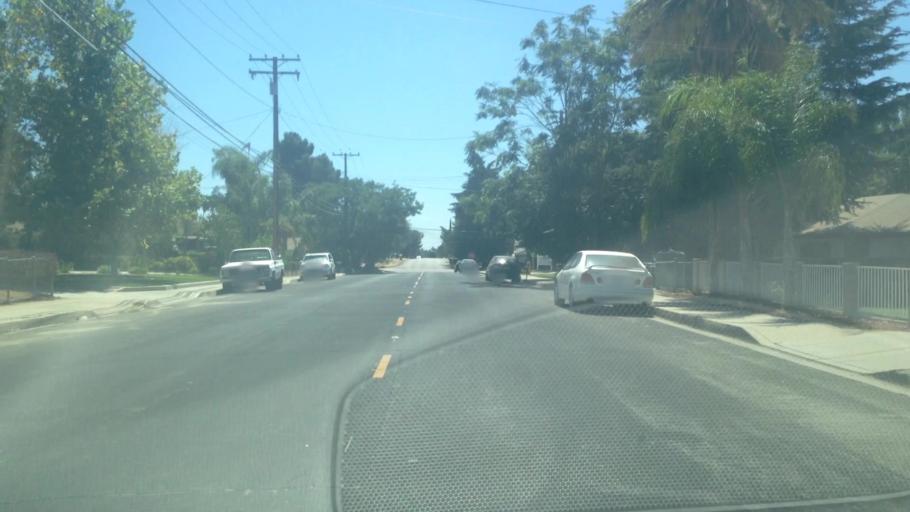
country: US
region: California
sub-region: San Bernardino County
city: Yucaipa
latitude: 34.0280
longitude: -117.0432
